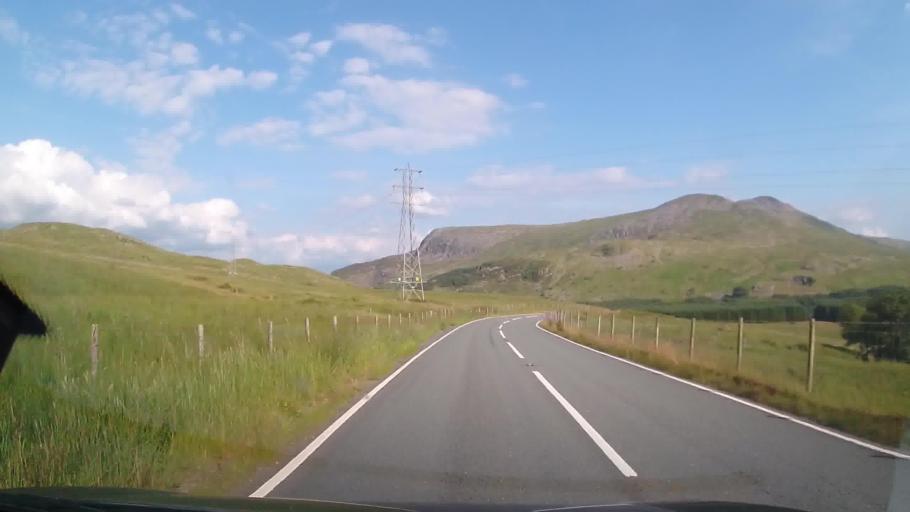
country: GB
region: Wales
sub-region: Conwy
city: Betws-y-Coed
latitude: 52.9414
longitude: -3.7702
